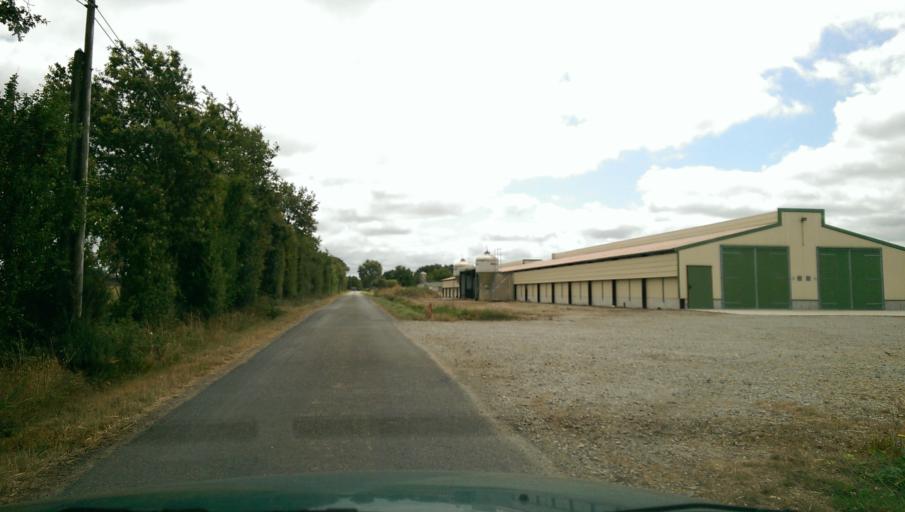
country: FR
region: Pays de la Loire
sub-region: Departement de la Loire-Atlantique
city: Vieillevigne
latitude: 46.9857
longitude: -1.4121
